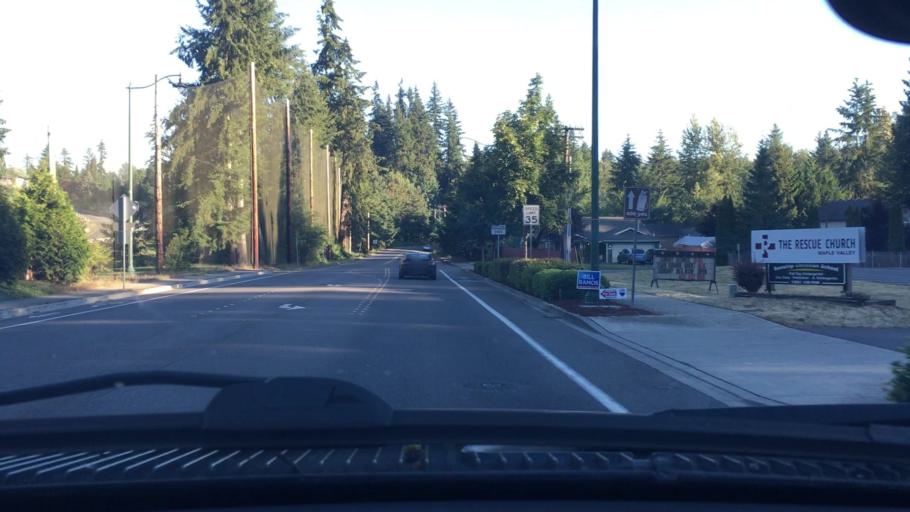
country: US
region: Washington
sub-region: King County
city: Maple Valley
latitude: 47.3789
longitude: -122.0482
